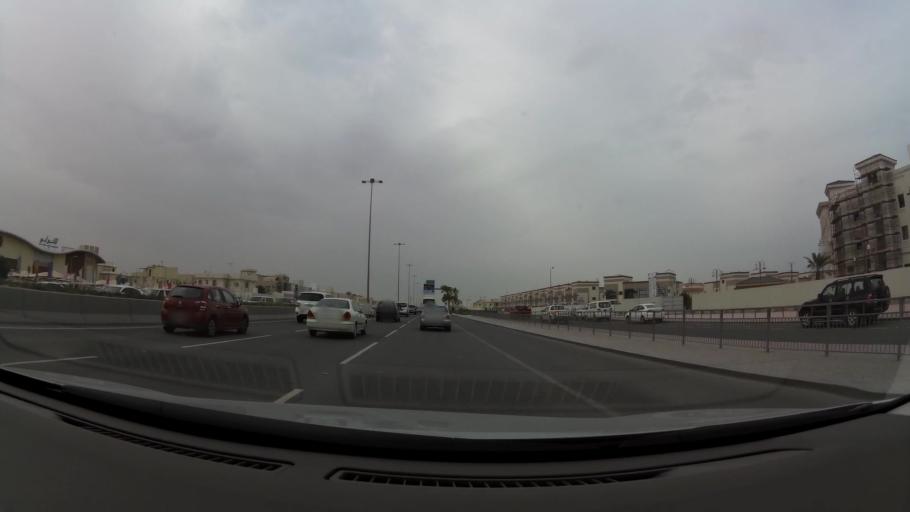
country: QA
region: Baladiyat ar Rayyan
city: Ar Rayyan
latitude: 25.3381
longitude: 51.4613
